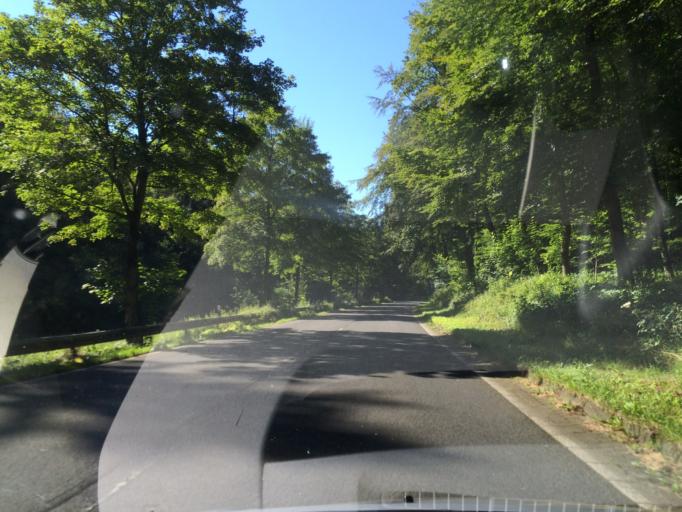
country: DE
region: North Rhine-Westphalia
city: Iserlohn
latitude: 51.3549
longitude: 7.6987
